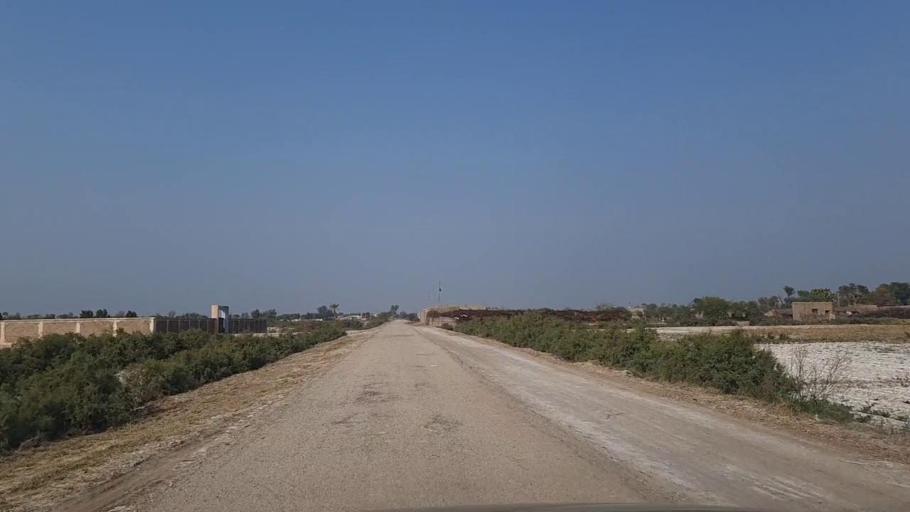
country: PK
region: Sindh
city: Daur
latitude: 26.4195
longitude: 68.4088
